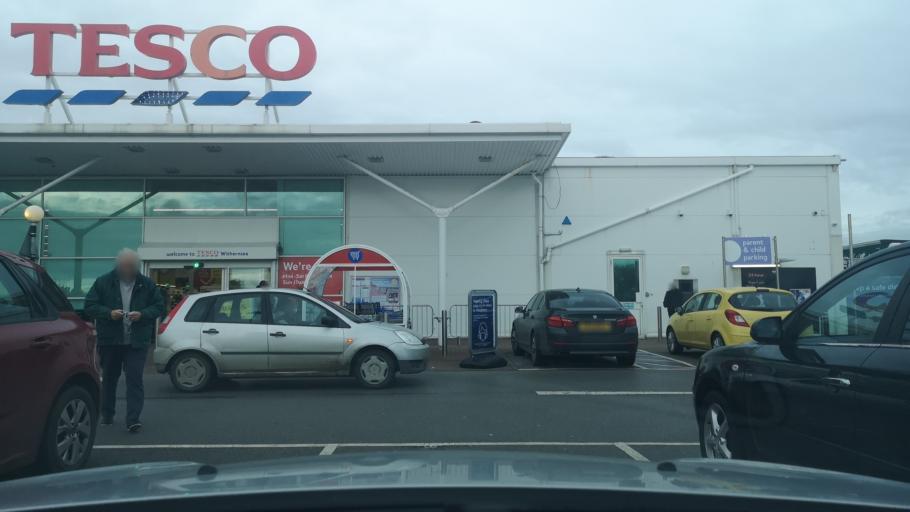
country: GB
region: England
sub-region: East Riding of Yorkshire
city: Withernsea
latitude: 53.7236
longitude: 0.0364
